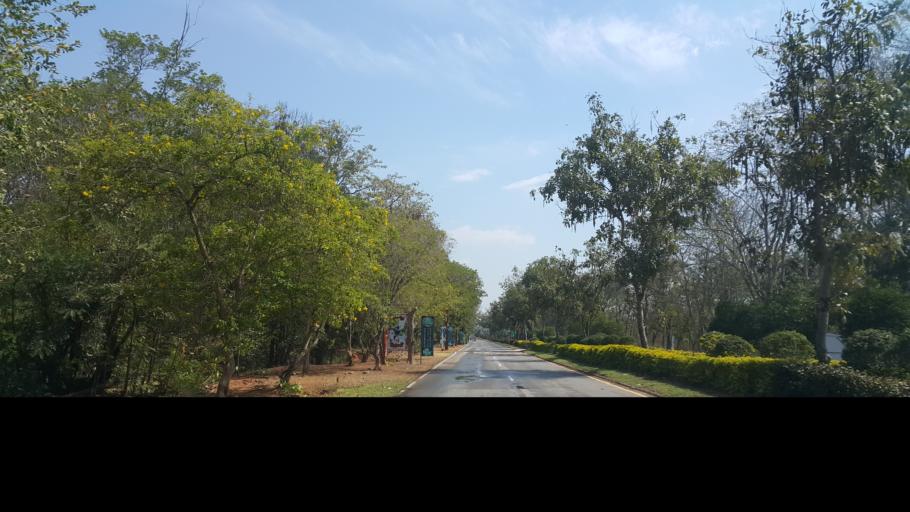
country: TH
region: Nakhon Ratchasima
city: Nakhon Ratchasima
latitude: 14.8502
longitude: 102.0807
